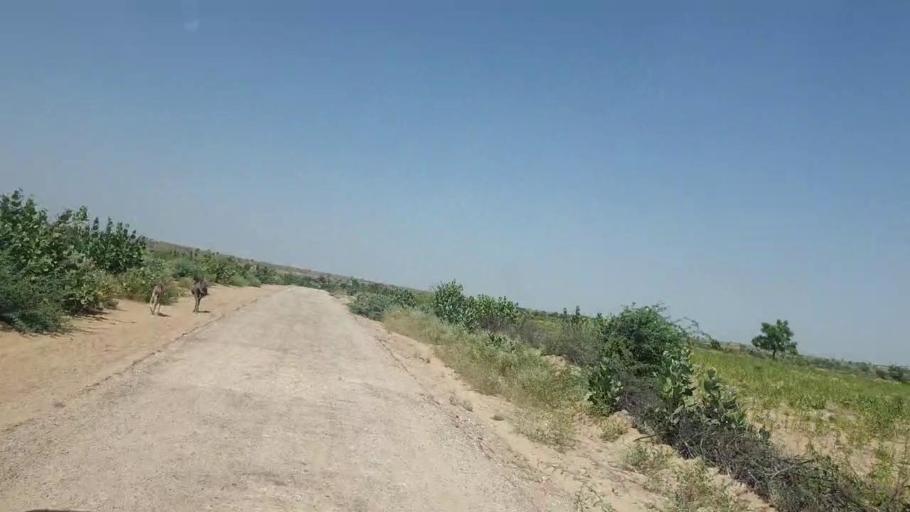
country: PK
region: Sindh
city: Chor
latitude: 25.3699
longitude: 70.3195
